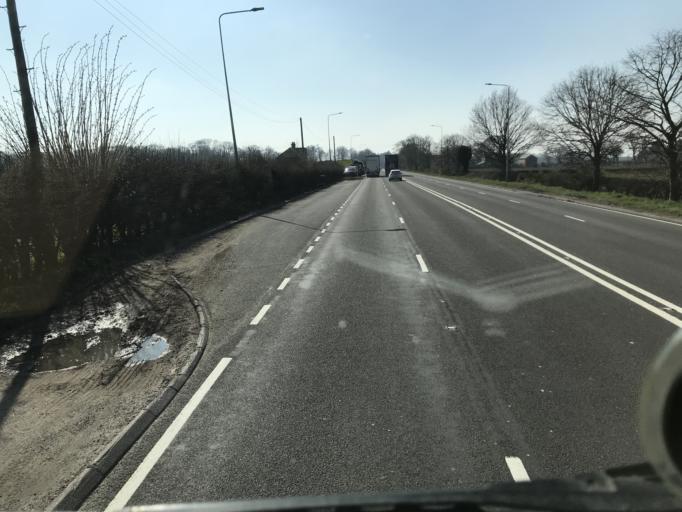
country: GB
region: England
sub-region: Cheshire East
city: Mere
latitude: 53.3060
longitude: -2.4184
